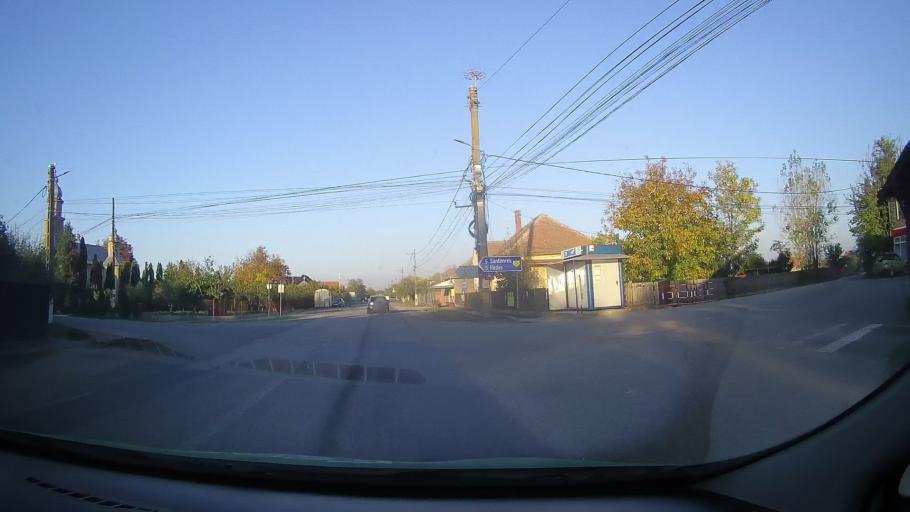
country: RO
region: Bihor
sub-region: Comuna Salard
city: Salard
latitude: 47.2171
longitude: 22.0322
